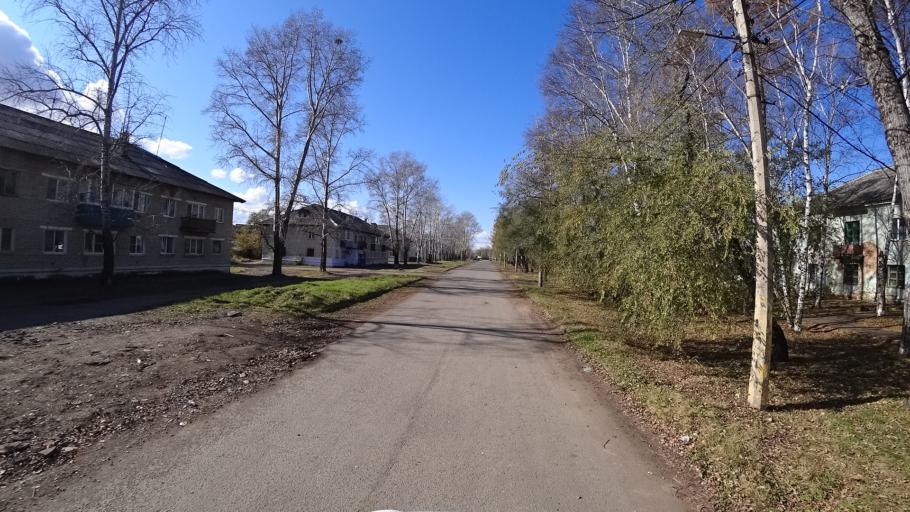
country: RU
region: Khabarovsk Krai
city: Amursk
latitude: 50.0993
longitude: 136.4969
